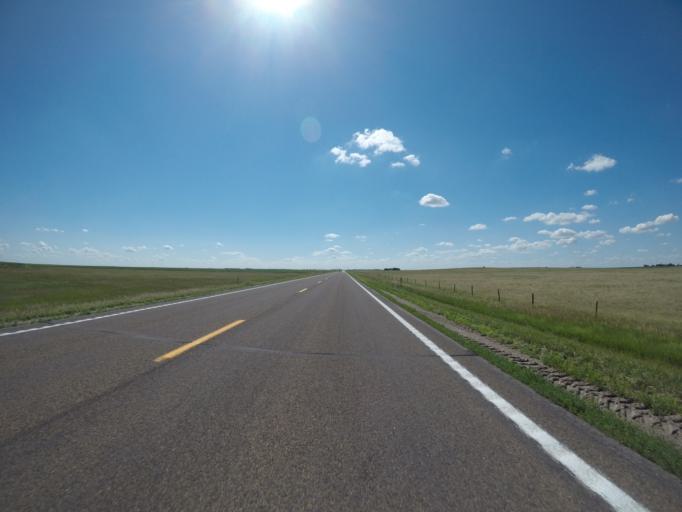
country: US
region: Nebraska
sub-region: Chase County
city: Imperial
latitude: 40.5377
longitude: -101.8637
